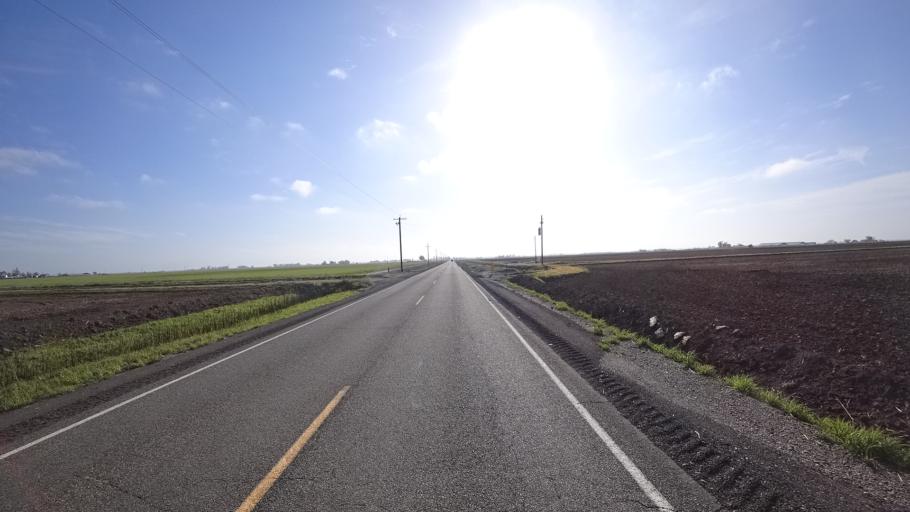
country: US
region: California
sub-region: Glenn County
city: Willows
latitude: 39.5828
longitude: -122.0942
